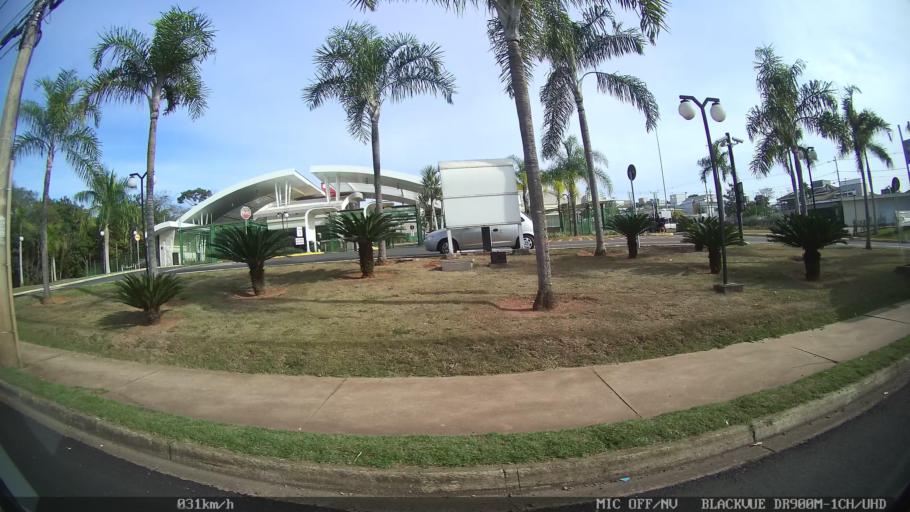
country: BR
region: Sao Paulo
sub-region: Piracicaba
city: Piracicaba
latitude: -22.7044
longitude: -47.6767
